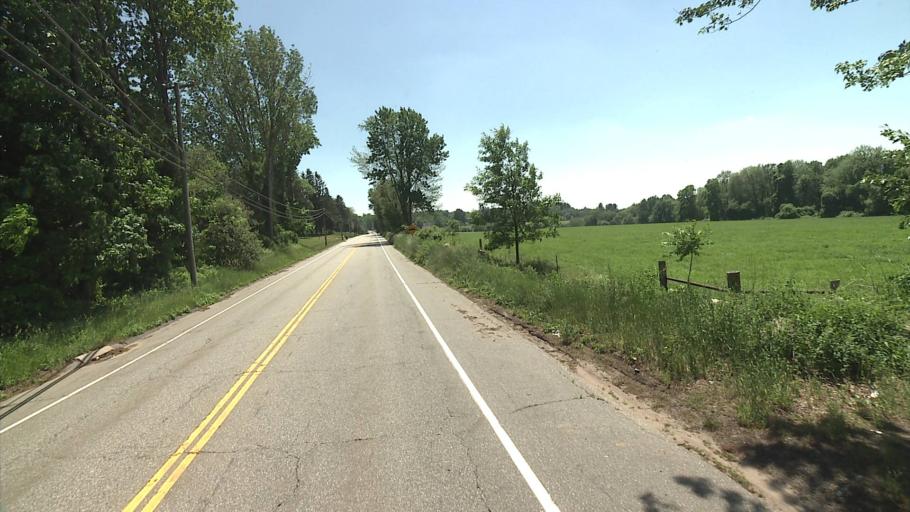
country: US
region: Connecticut
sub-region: Tolland County
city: Tolland
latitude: 41.8774
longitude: -72.4049
